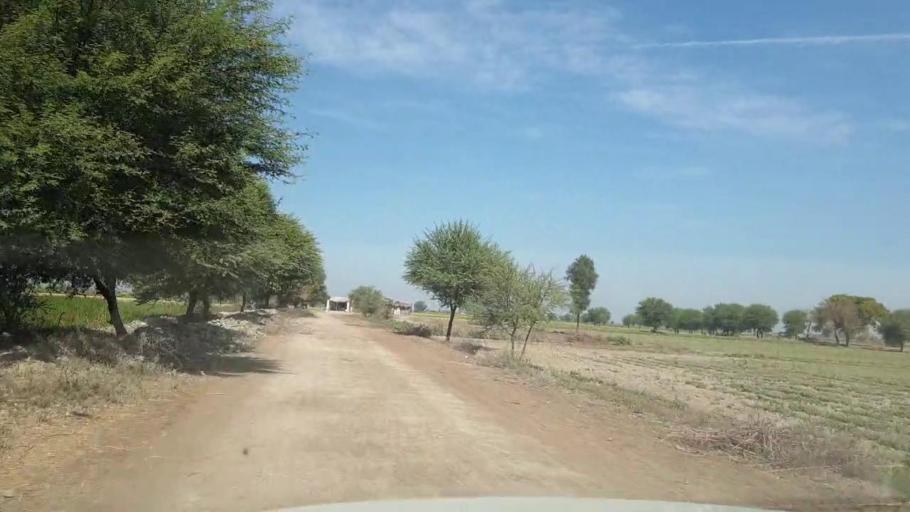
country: PK
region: Sindh
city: Pithoro
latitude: 25.6299
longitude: 69.2021
